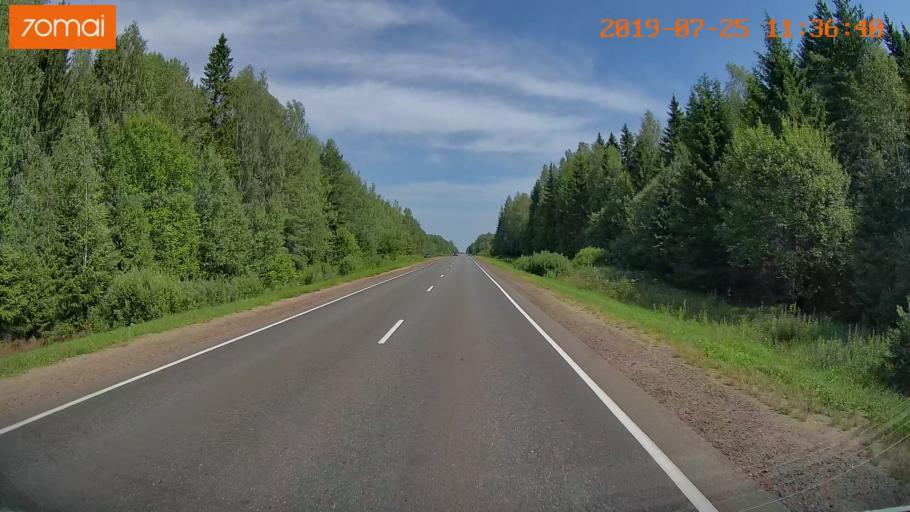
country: RU
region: Ivanovo
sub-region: Privolzhskiy Rayon
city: Ples
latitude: 57.4253
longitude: 41.4532
